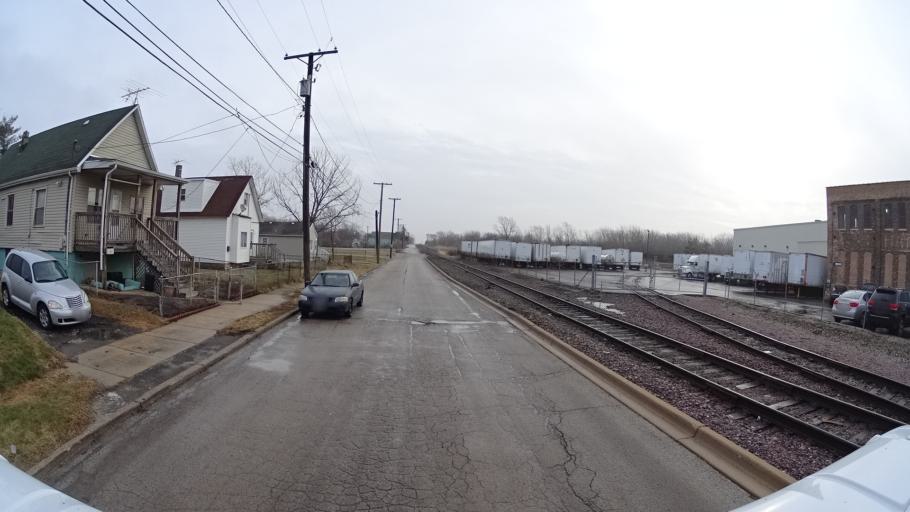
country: US
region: Illinois
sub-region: Cook County
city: Chicago Heights
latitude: 41.5008
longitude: -87.6268
